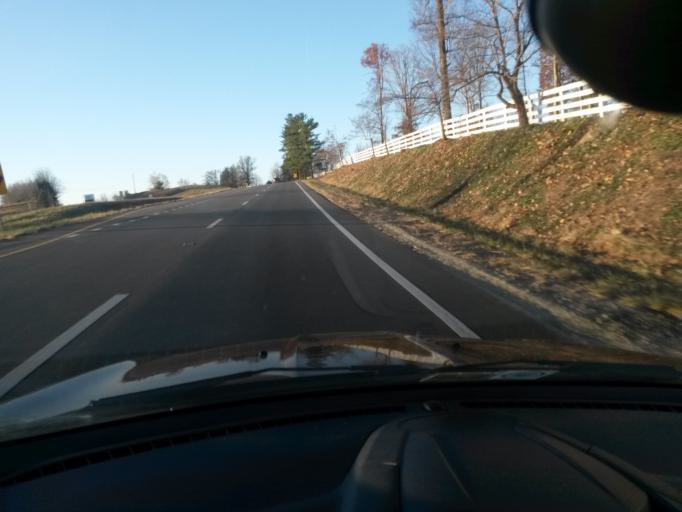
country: US
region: Virginia
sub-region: Franklin County
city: Henry Fork
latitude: 36.8752
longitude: -79.8708
